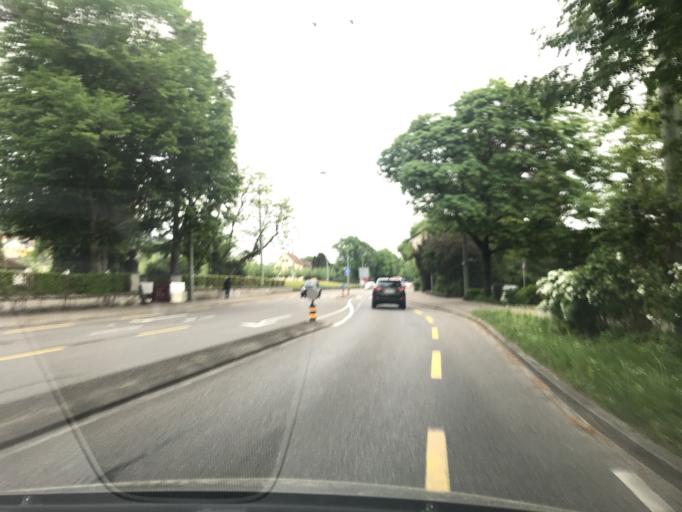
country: CH
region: Zurich
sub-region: Bezirk Winterthur
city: Wuelflingen (Kreis 6) / Lindenplatz
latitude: 47.5110
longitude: 8.6986
